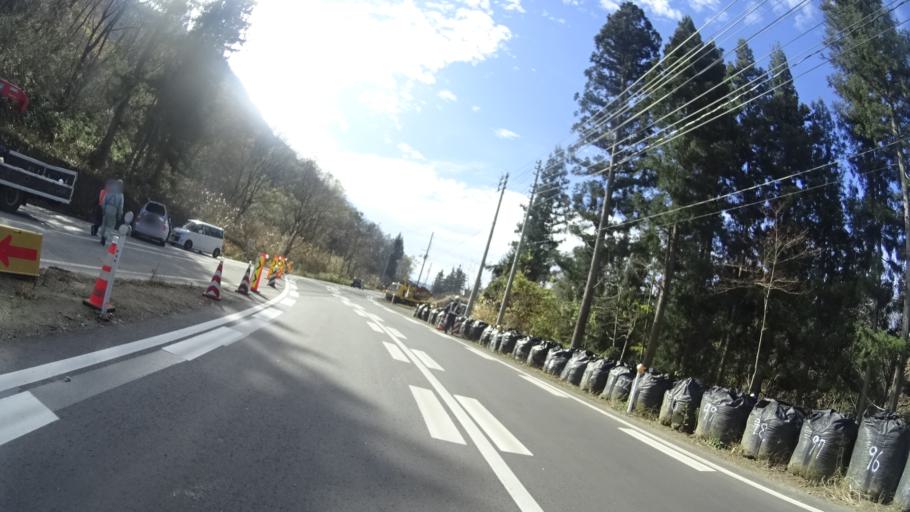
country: JP
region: Niigata
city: Ojiya
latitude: 37.2712
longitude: 138.9866
